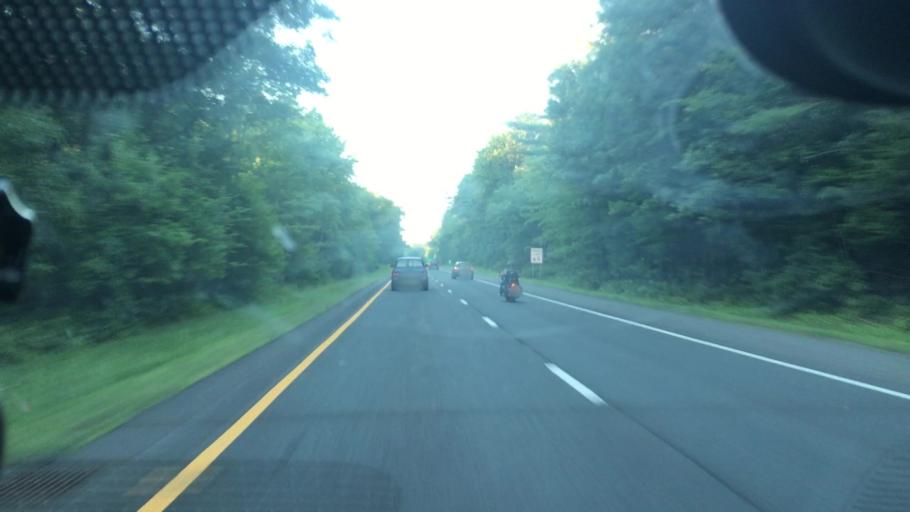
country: US
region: Massachusetts
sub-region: Franklin County
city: Turners Falls
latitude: 42.6246
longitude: -72.5856
